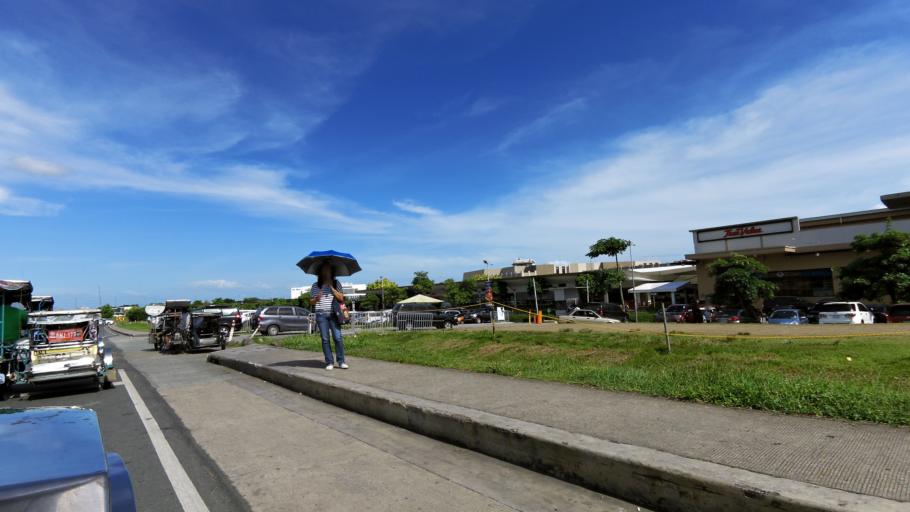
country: PH
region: Calabarzon
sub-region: Province of Cavite
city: Puting Kahoy
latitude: 14.2379
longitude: 121.0554
